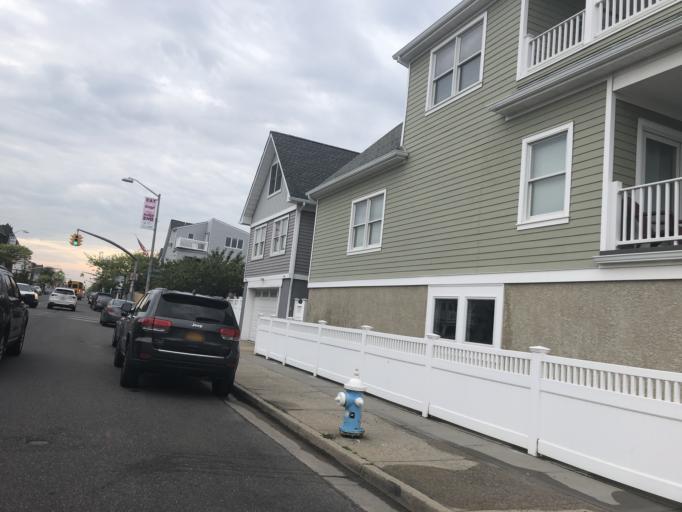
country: US
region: New York
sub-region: Nassau County
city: Harbor Isle
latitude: 40.5861
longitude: -73.6897
